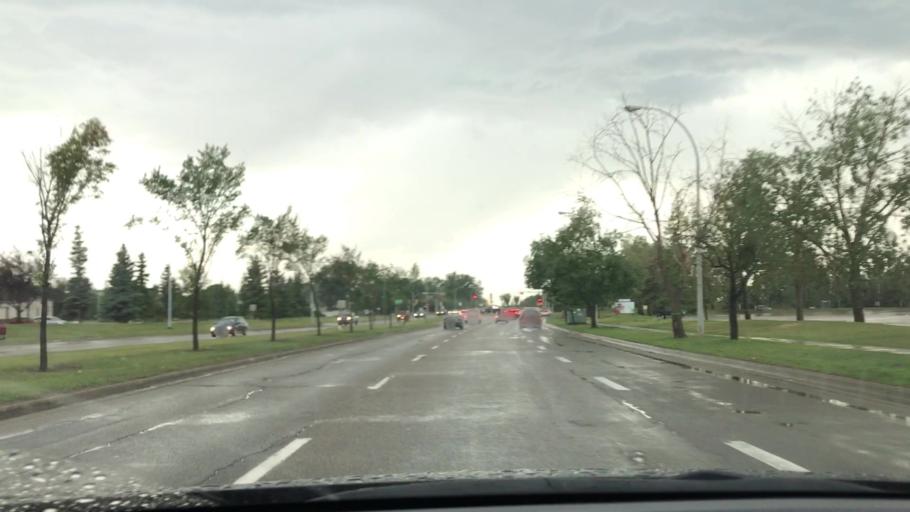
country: CA
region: Alberta
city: Edmonton
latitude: 53.4537
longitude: -113.4311
